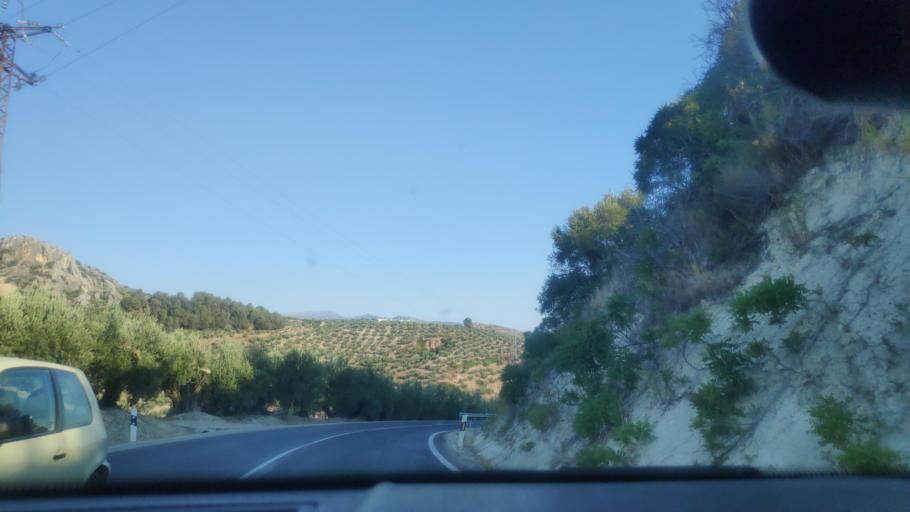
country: ES
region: Andalusia
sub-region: Provincia de Jaen
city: Jaen
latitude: 37.7543
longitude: -3.7905
